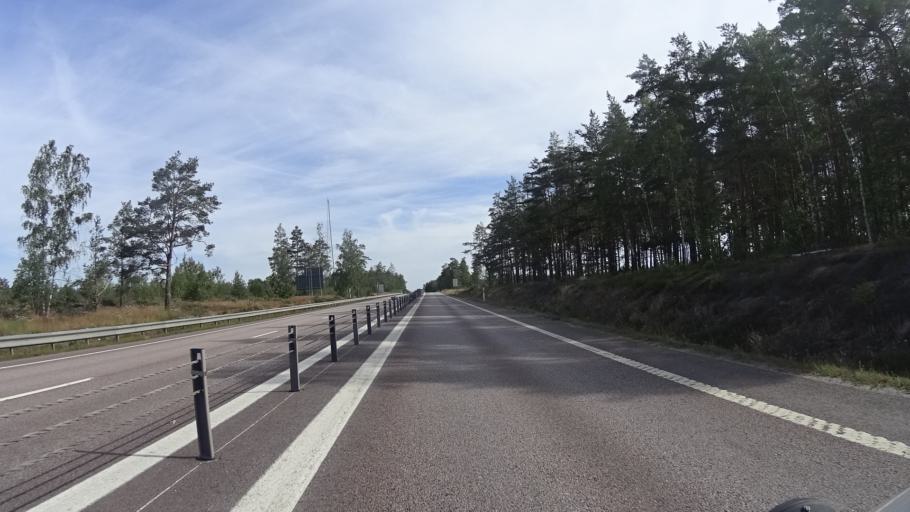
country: SE
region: Kalmar
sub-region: Oskarshamns Kommun
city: Oskarshamn
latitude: 57.4019
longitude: 16.4804
